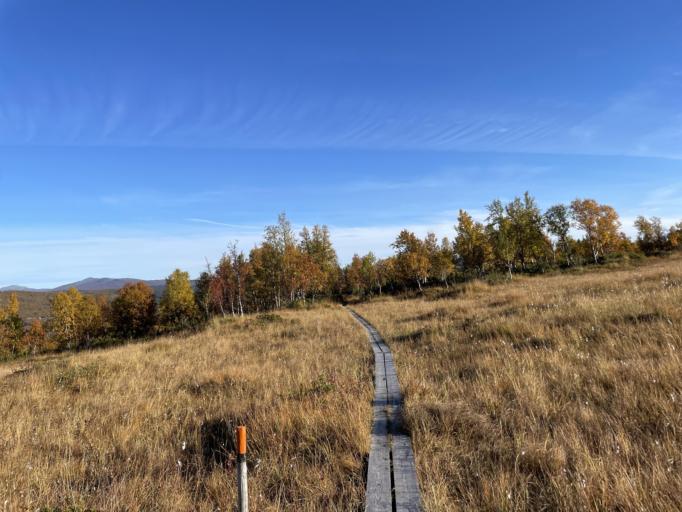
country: NO
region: Sor-Trondelag
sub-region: Tydal
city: Aas
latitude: 62.6385
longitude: 12.3918
